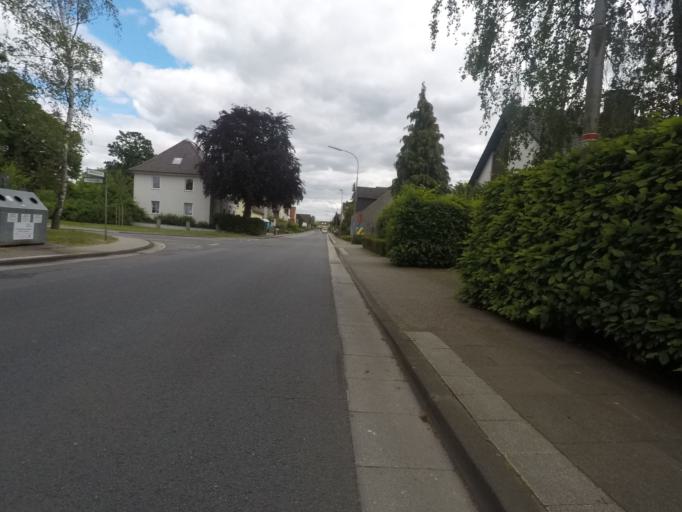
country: DE
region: North Rhine-Westphalia
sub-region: Regierungsbezirk Detmold
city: Herford
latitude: 52.1143
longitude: 8.6910
